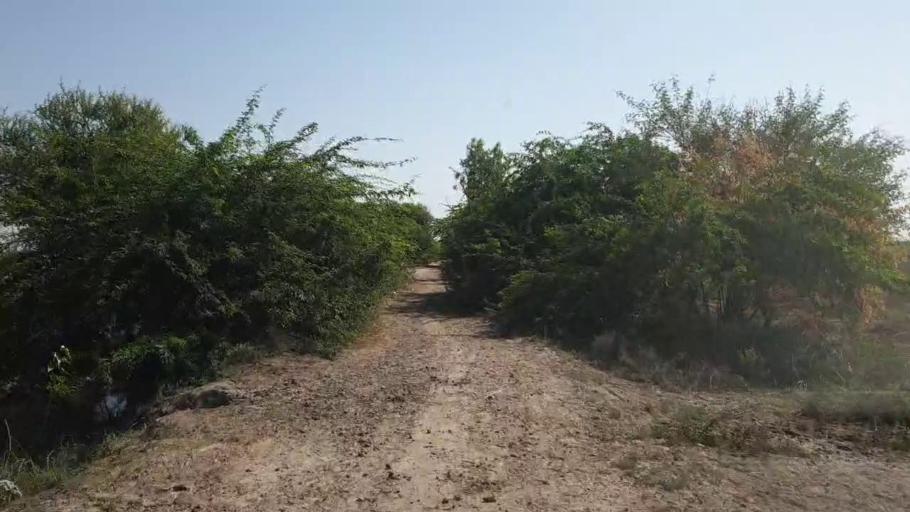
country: PK
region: Sindh
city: Kadhan
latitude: 24.5935
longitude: 69.0067
